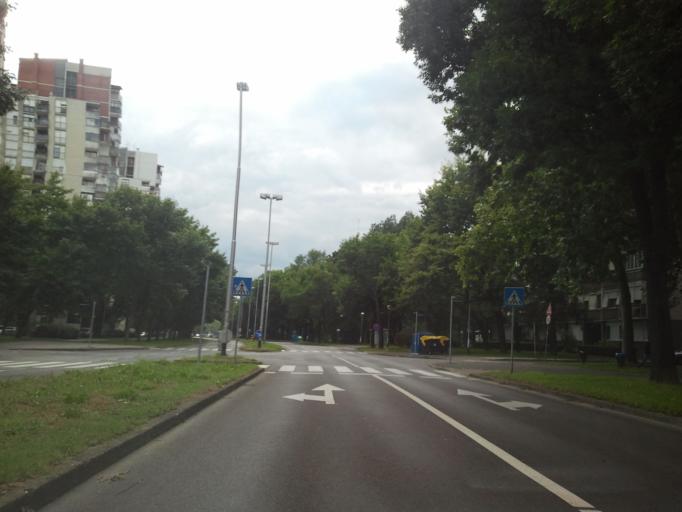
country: HR
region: Grad Zagreb
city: Novi Zagreb
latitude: 45.7730
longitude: 15.9990
